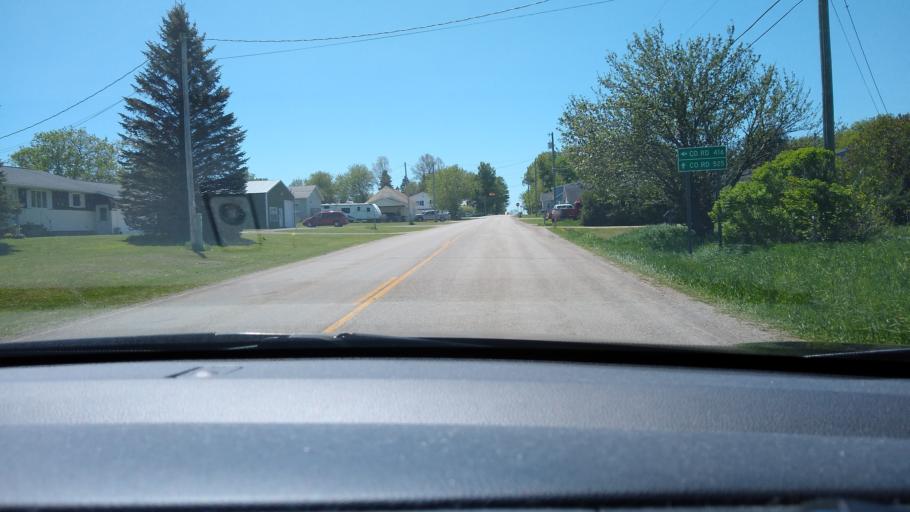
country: US
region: Michigan
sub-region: Delta County
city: Escanaba
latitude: 45.8276
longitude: -87.1831
